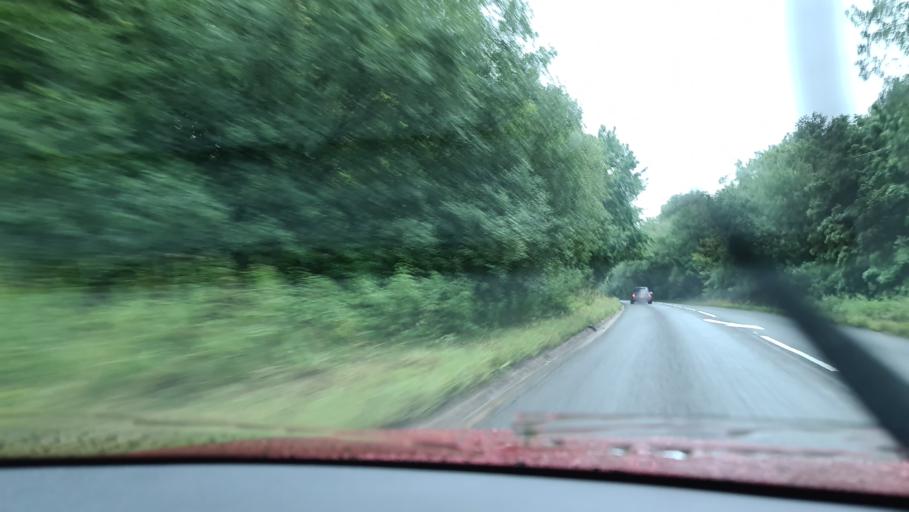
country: GB
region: England
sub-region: Buckinghamshire
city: Amersham
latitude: 51.6508
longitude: -0.6176
